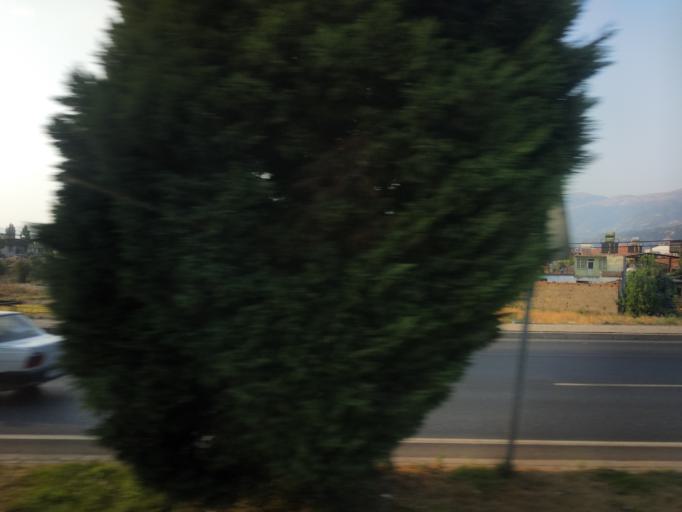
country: TR
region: Manisa
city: Salihli
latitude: 38.4914
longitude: 28.1651
